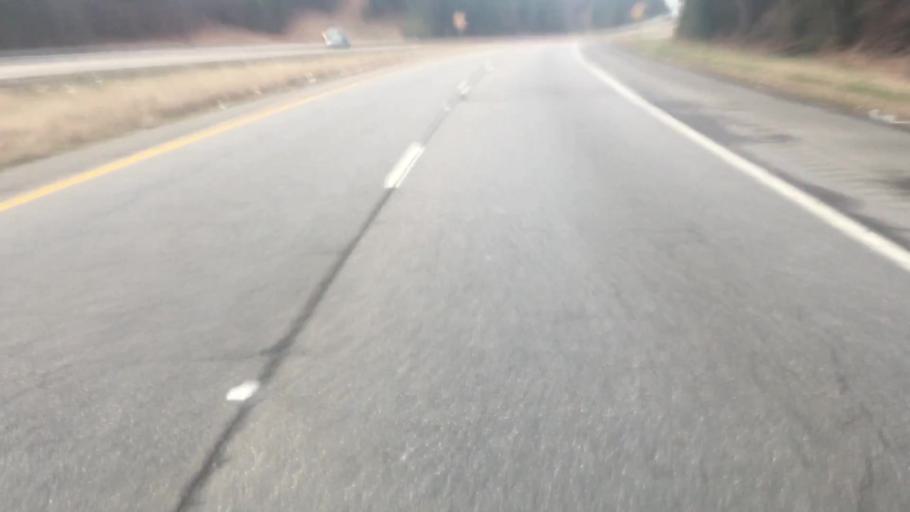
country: US
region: Alabama
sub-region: Walker County
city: Sumiton
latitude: 33.7725
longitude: -87.0734
